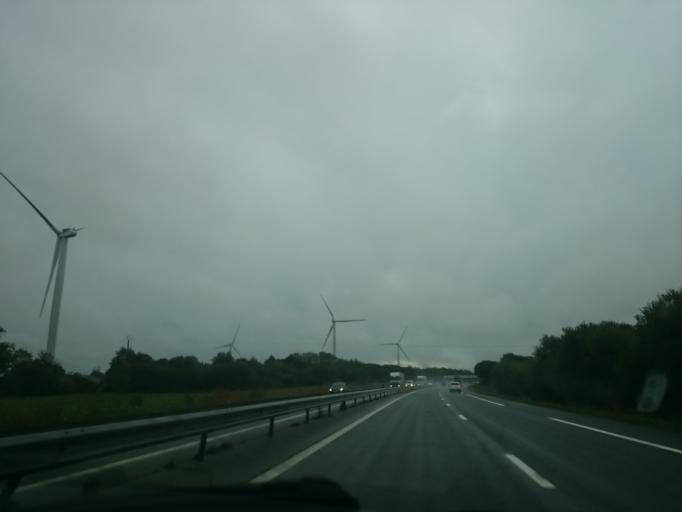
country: FR
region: Pays de la Loire
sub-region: Departement de la Loire-Atlantique
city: Sainte-Anne-sur-Brivet
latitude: 47.4158
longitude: -2.0304
